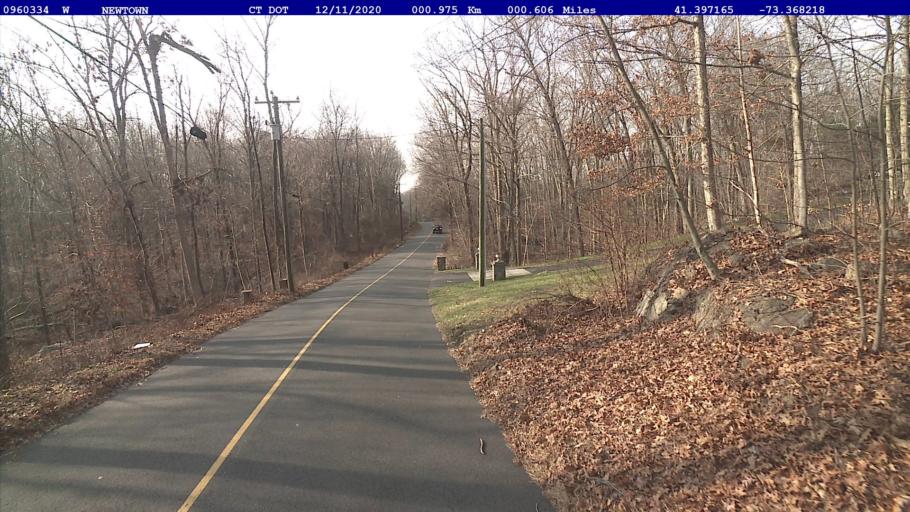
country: US
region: Connecticut
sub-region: Fairfield County
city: Bethel
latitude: 41.3972
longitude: -73.3682
